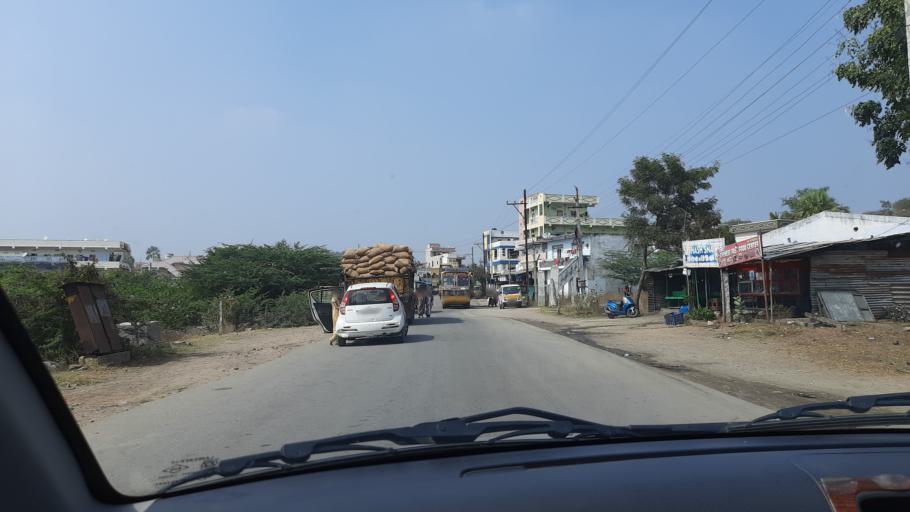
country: IN
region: Telangana
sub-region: Rangareddi
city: Lal Bahadur Nagar
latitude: 17.2706
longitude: 78.6710
